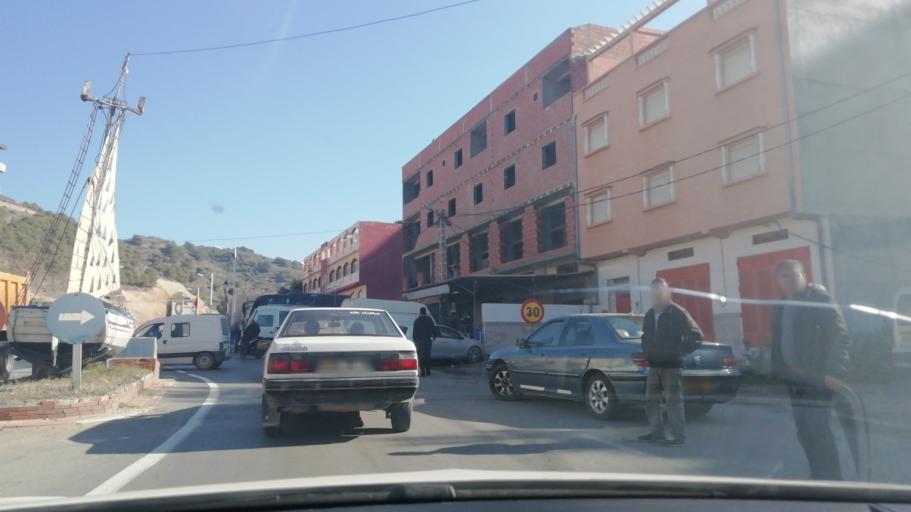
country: DZ
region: Tlemcen
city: Nedroma
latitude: 35.1025
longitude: -1.8557
